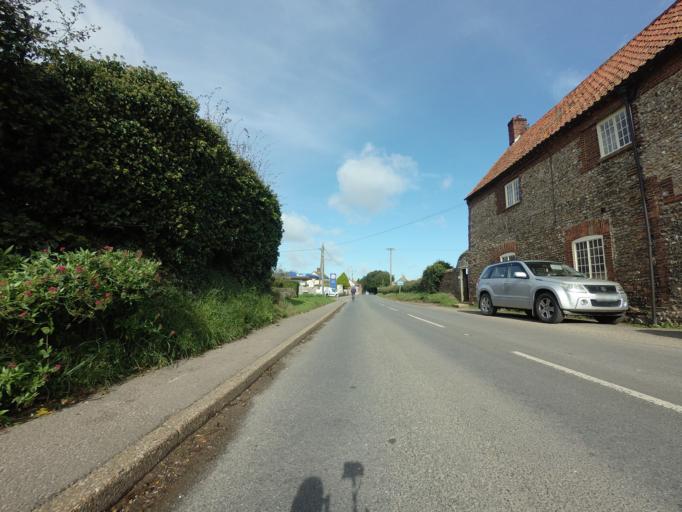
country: GB
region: England
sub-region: Norfolk
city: Wells-next-the-Sea
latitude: 52.9429
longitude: 0.7313
